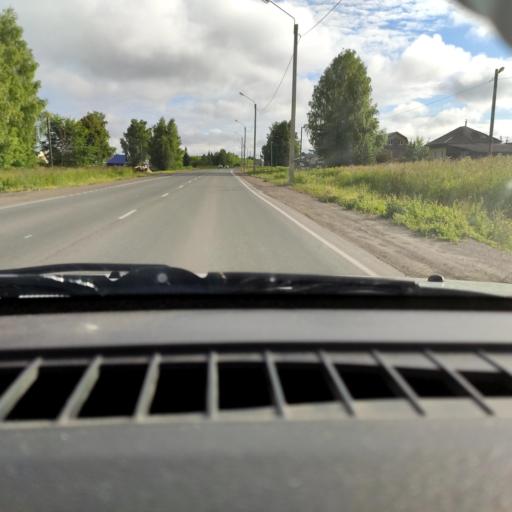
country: RU
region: Perm
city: Kungur
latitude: 57.3756
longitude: 56.9669
